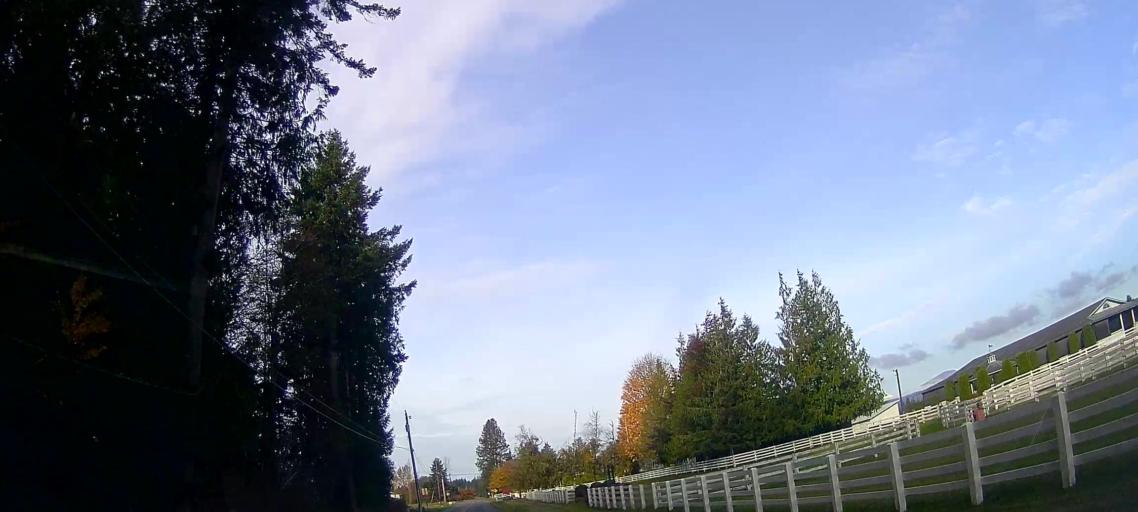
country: US
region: Washington
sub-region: Snohomish County
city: Stanwood
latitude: 48.2670
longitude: -122.3414
